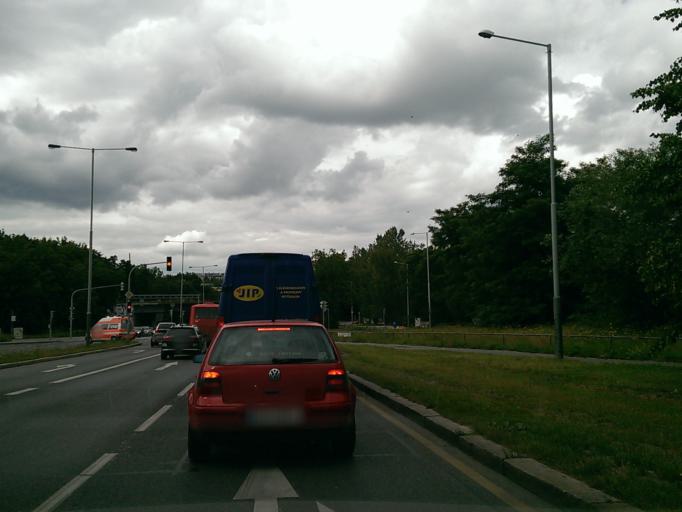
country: CZ
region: Praha
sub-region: Praha 4
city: Hodkovicky
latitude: 50.0342
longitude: 14.4557
